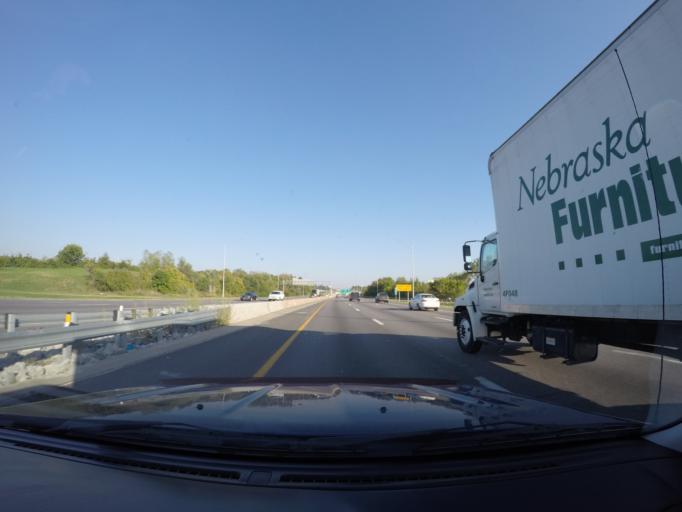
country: US
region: Missouri
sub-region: Jackson County
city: Raytown
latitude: 39.0628
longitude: -94.4984
